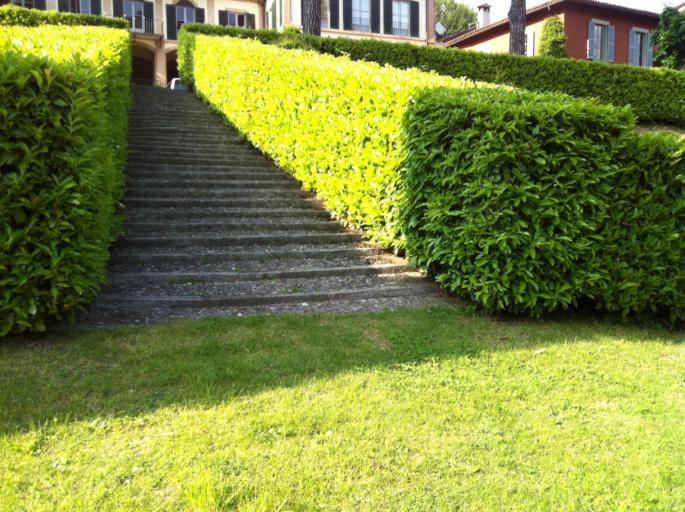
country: IT
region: Lombardy
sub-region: Provincia di Como
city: Menaggio
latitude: 46.0268
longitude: 9.2308
